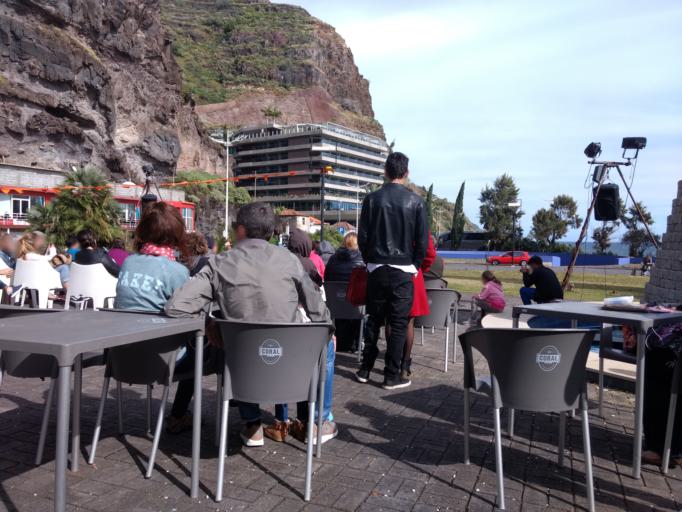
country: PT
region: Madeira
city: Calheta
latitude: 32.7173
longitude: -17.1699
